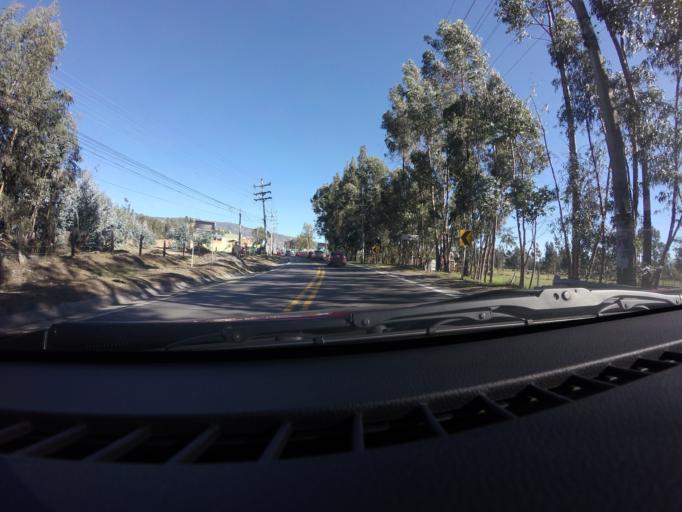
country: CO
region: Cundinamarca
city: Ubate
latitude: 5.2950
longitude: -73.8153
